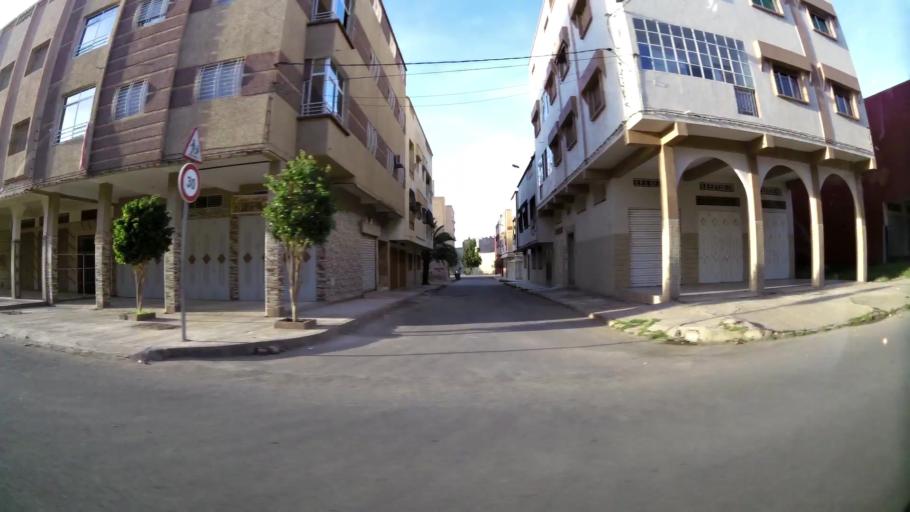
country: MA
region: Oriental
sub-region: Oujda-Angad
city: Oujda
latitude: 34.6768
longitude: -1.8935
